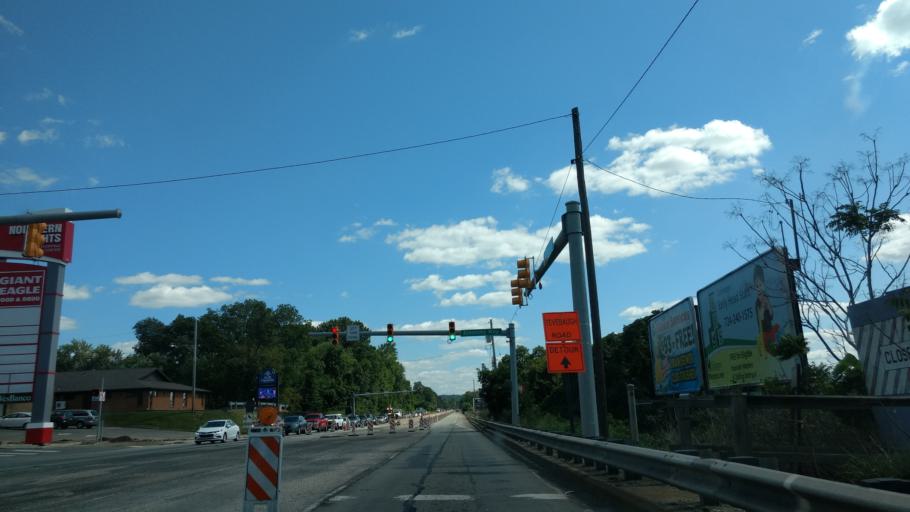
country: US
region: Pennsylvania
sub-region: Beaver County
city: Conway
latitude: 40.6557
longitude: -80.2376
